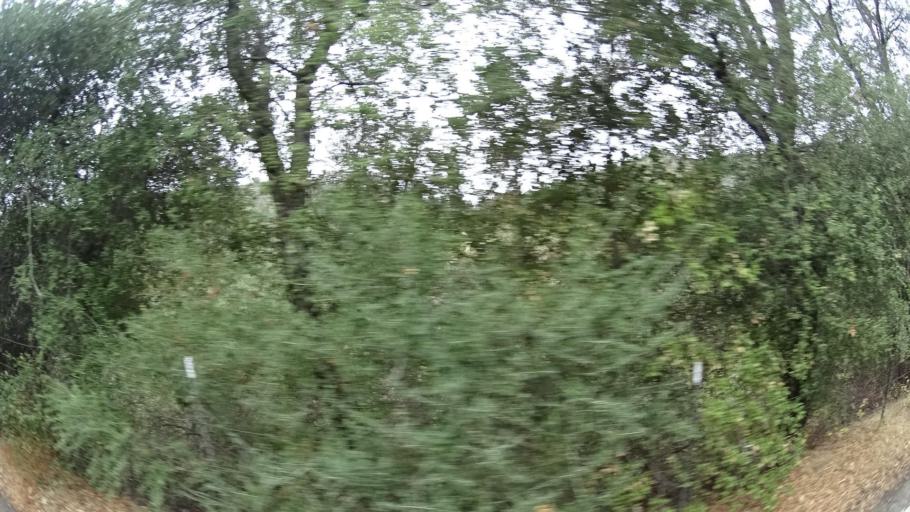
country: US
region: California
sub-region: San Diego County
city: Julian
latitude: 33.0238
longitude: -116.6362
